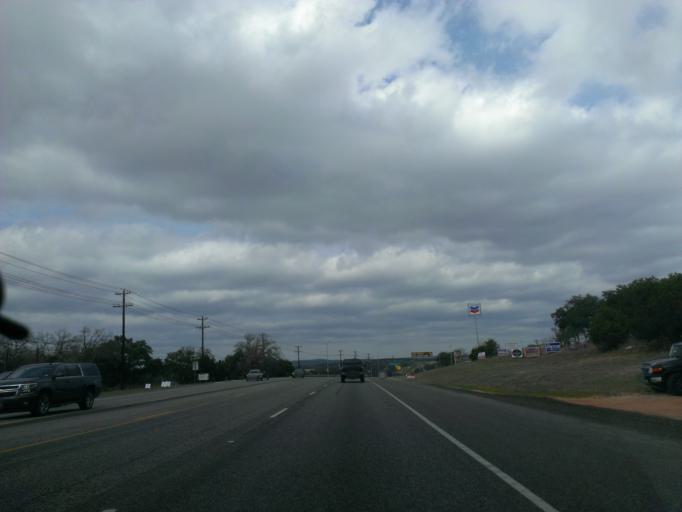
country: US
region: Texas
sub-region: Travis County
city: Briarcliff
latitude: 30.3834
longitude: -98.0848
